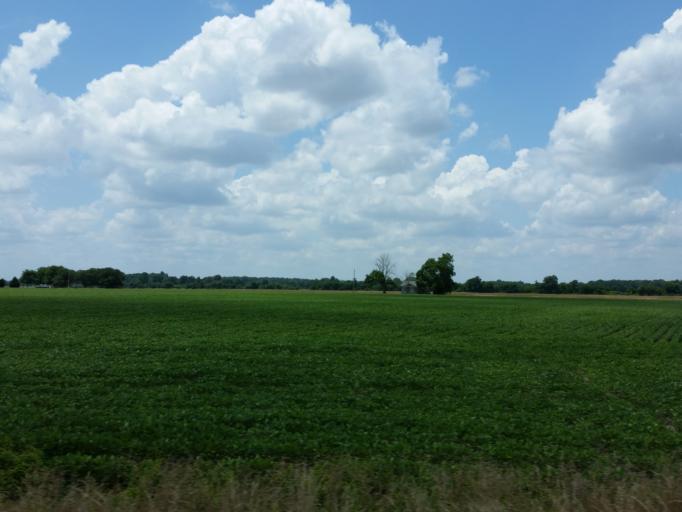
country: US
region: Tennessee
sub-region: Lake County
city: Ridgely
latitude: 36.1809
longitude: -89.4476
